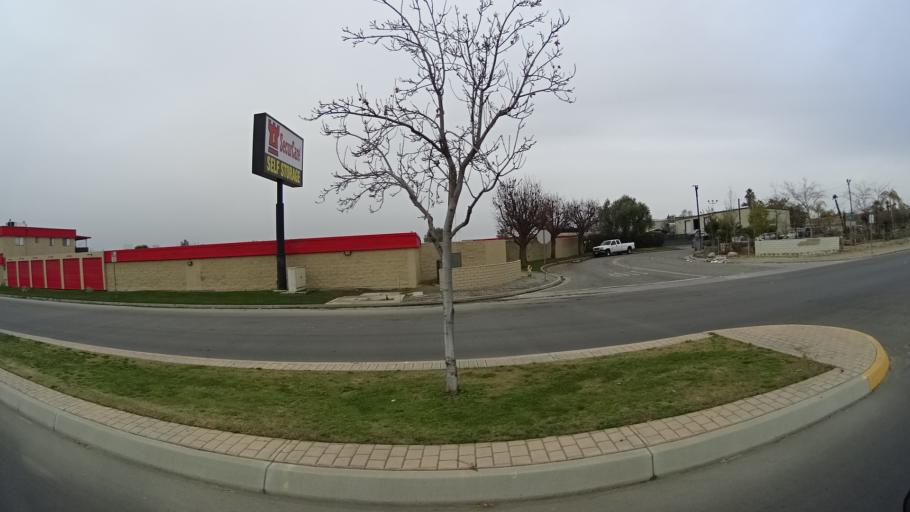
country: US
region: California
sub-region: Kern County
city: Bakersfield
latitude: 35.3504
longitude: -118.9497
